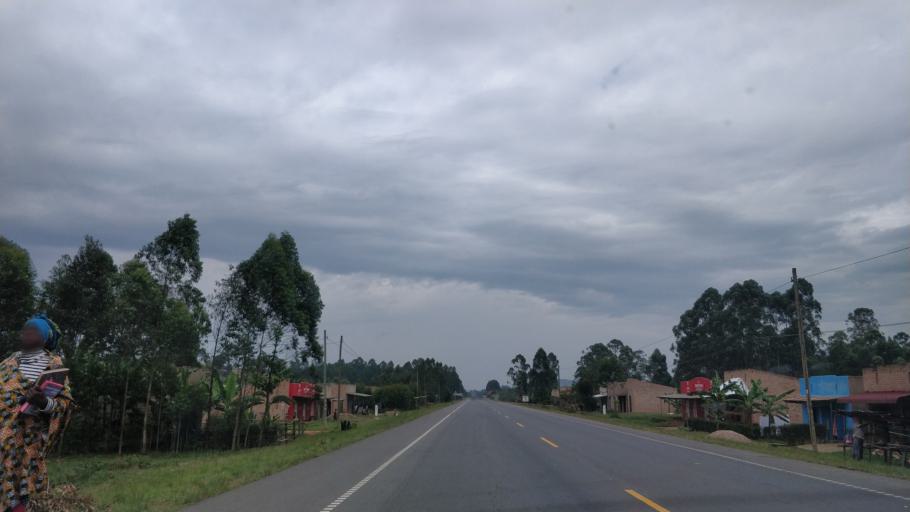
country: UG
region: Western Region
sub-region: Sheema District
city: Kibingo
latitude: -0.6724
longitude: 30.4292
